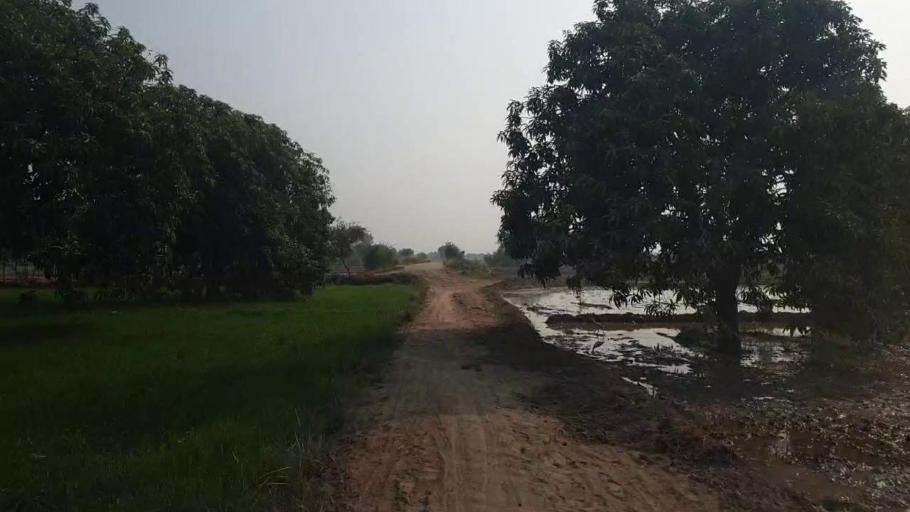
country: PK
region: Sindh
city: Tando Jam
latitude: 25.3279
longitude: 68.5216
